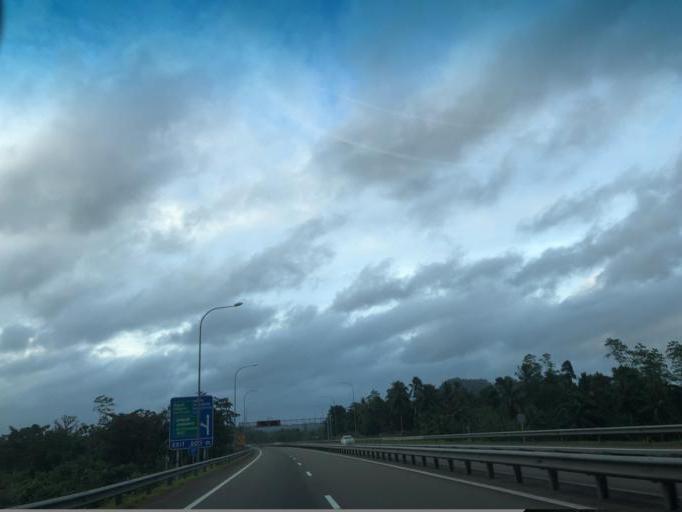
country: LK
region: Western
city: Horawala Junction
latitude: 6.4451
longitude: 80.0923
